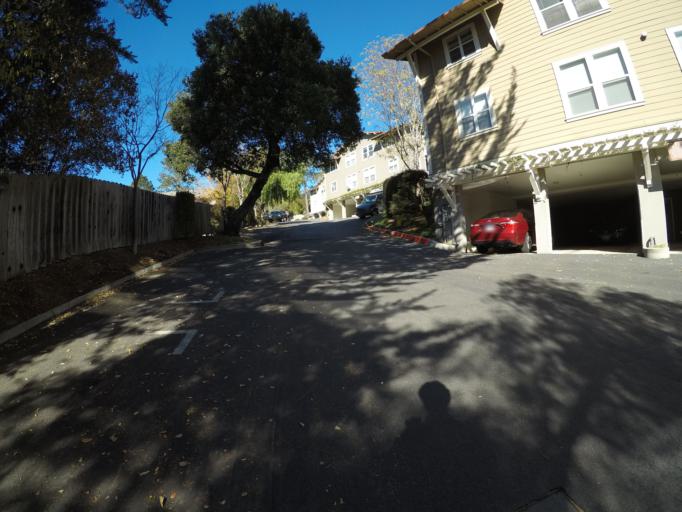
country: US
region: California
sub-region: Santa Cruz County
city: Scotts Valley
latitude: 37.0477
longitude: -122.0214
